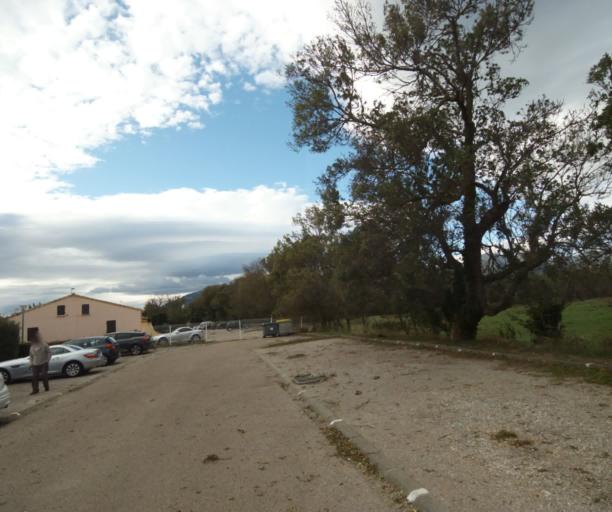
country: FR
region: Languedoc-Roussillon
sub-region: Departement des Pyrenees-Orientales
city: Argelers
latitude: 42.5628
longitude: 3.0397
